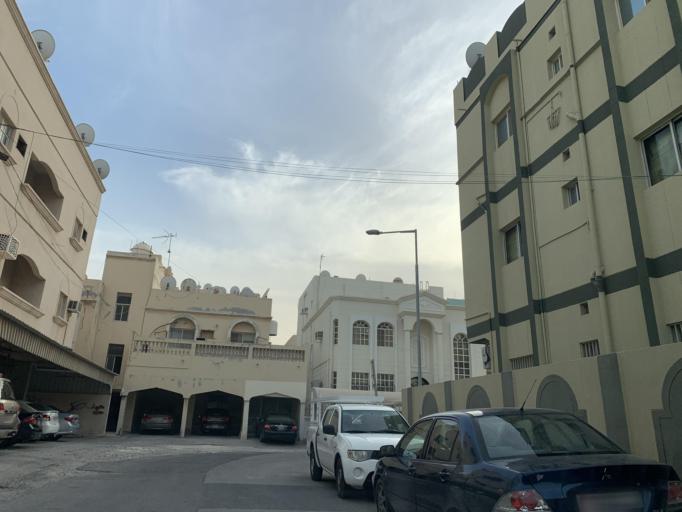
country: BH
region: Northern
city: Ar Rifa'
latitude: 26.1208
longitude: 50.5809
